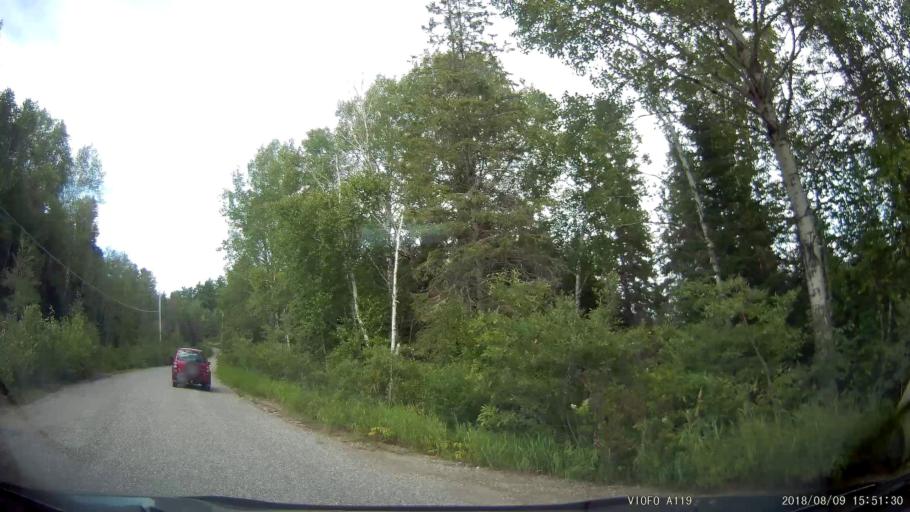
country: CA
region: Ontario
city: Rayside-Balfour
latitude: 46.5939
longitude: -81.5325
